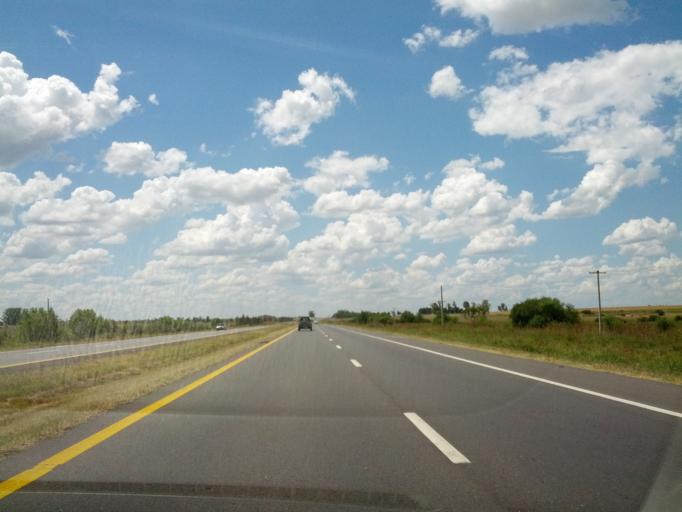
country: AR
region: Entre Rios
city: Gualeguaychu
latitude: -32.8888
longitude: -58.5503
